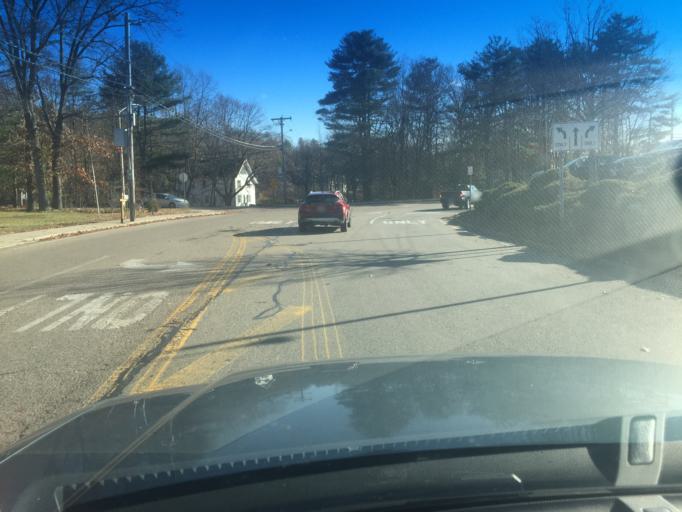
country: US
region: Massachusetts
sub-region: Norfolk County
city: Franklin
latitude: 42.0914
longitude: -71.4231
